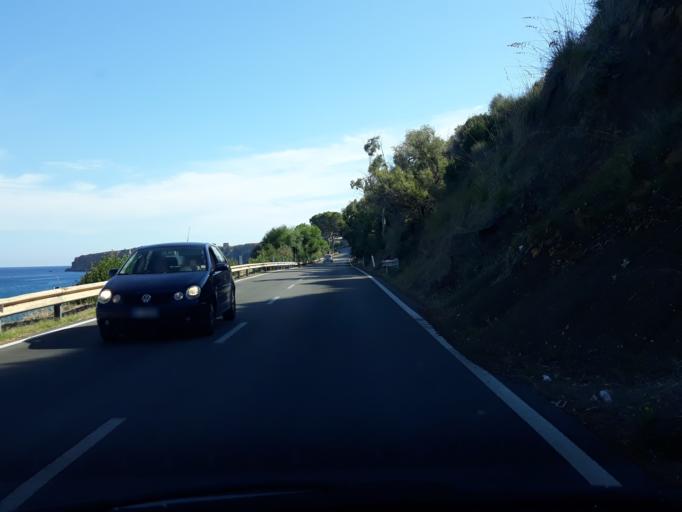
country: IT
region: Sicily
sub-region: Palermo
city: Pollina
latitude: 38.0183
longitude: 14.1317
